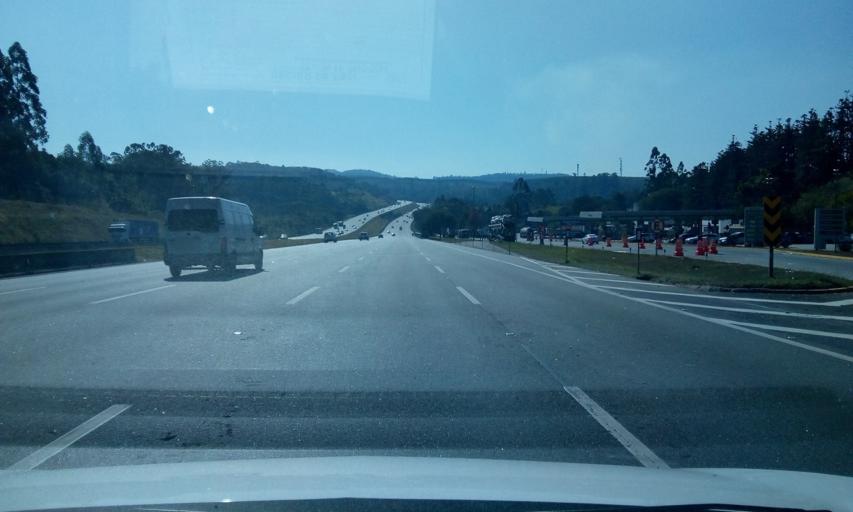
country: BR
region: Sao Paulo
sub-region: Caieiras
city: Caieiras
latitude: -23.3966
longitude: -46.7678
